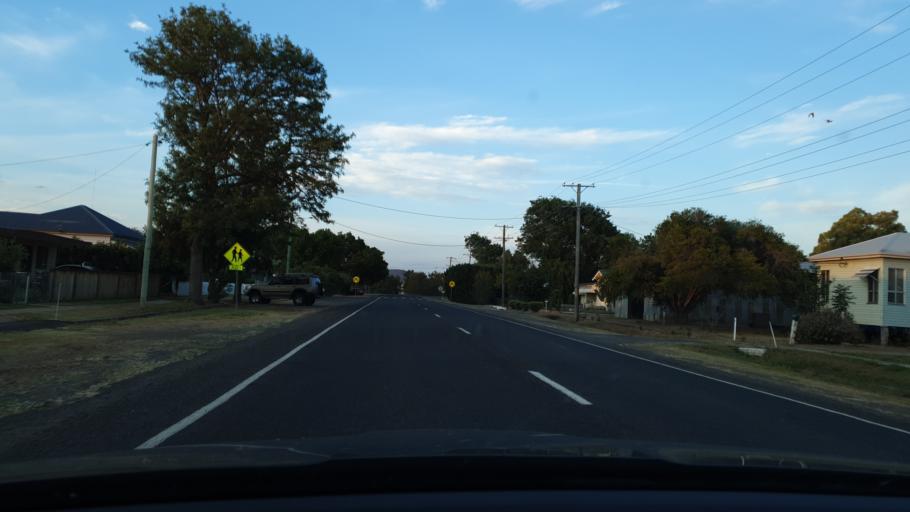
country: AU
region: Queensland
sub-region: Southern Downs
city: Warwick
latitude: -28.0330
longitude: 151.9808
